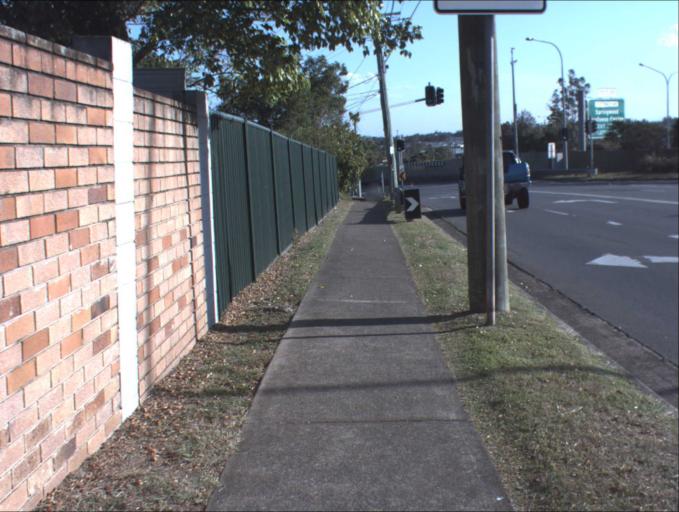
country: AU
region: Queensland
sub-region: Logan
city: Springwood
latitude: -27.6064
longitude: 153.1201
